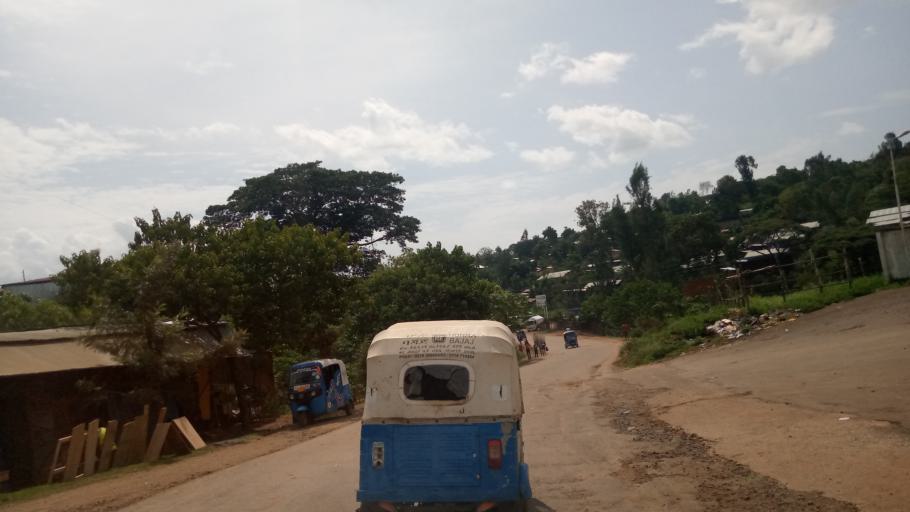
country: ET
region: Oromiya
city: Agaro
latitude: 7.8534
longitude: 36.5932
